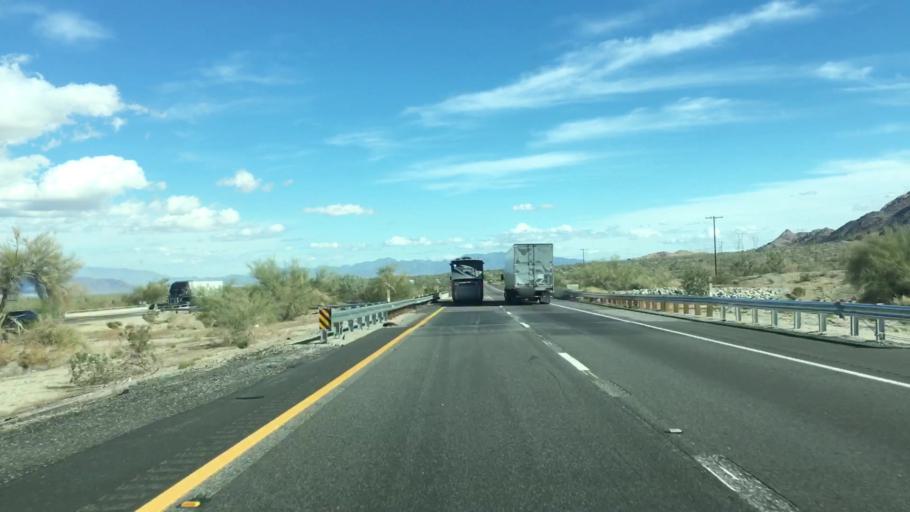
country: US
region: California
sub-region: Imperial County
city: Niland
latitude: 33.6901
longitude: -115.5076
